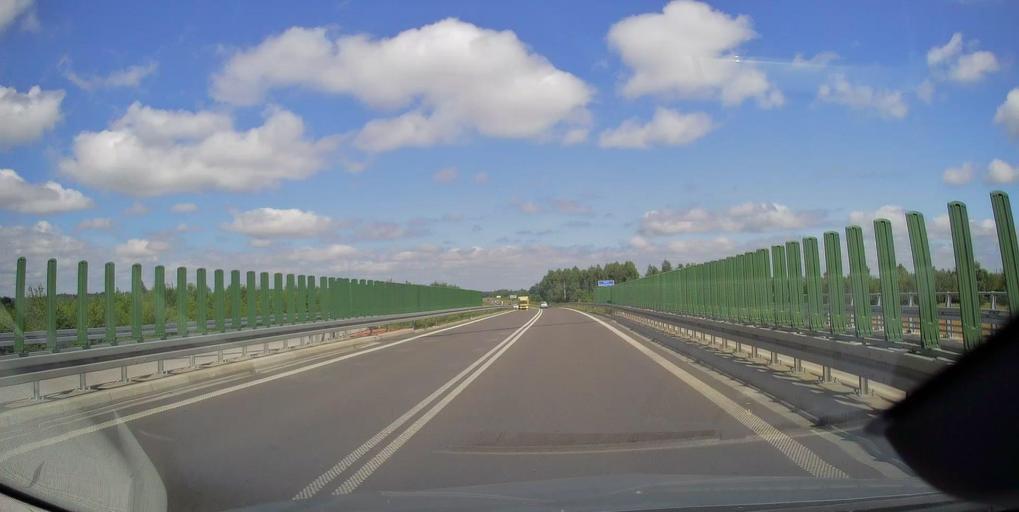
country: PL
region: Subcarpathian Voivodeship
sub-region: Powiat mielecki
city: Mielec
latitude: 50.3413
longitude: 21.4945
